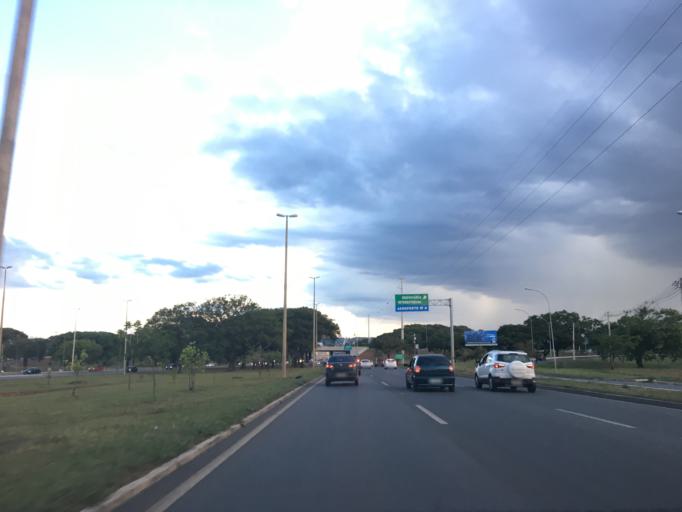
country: BR
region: Federal District
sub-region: Brasilia
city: Brasilia
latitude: -15.8372
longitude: -47.9530
